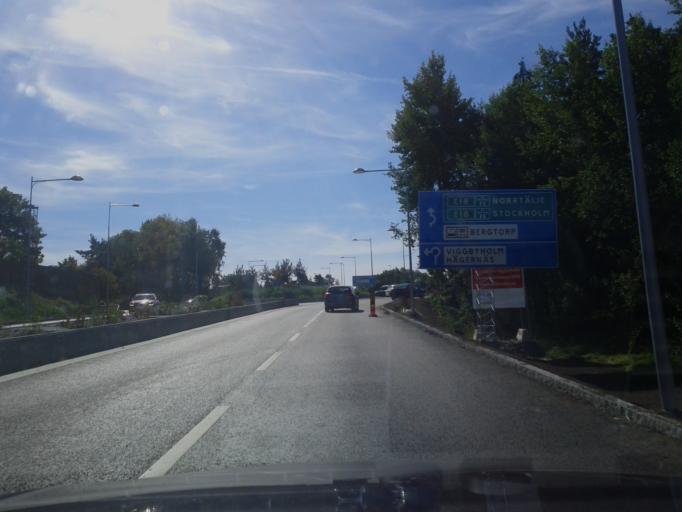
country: SE
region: Stockholm
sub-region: Taby Kommun
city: Taby
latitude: 59.4457
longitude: 18.0955
